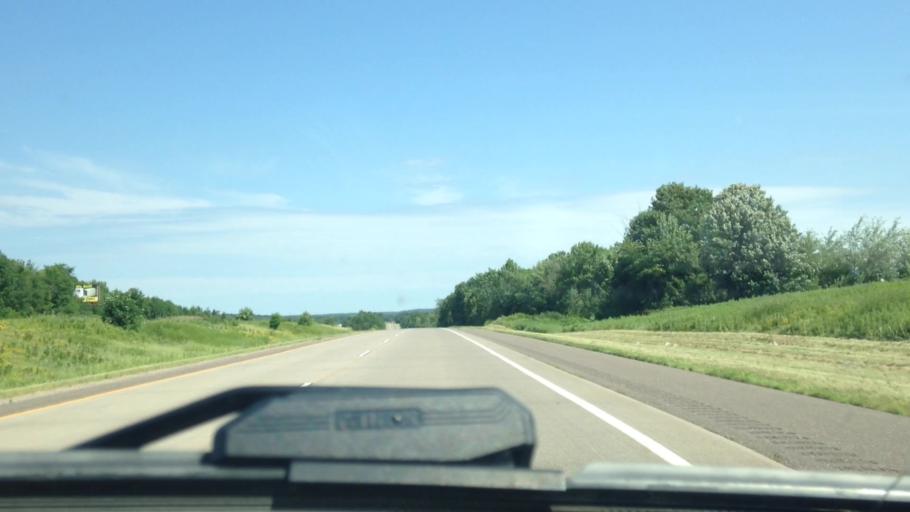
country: US
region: Wisconsin
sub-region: Barron County
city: Rice Lake
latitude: 45.5346
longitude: -91.7600
